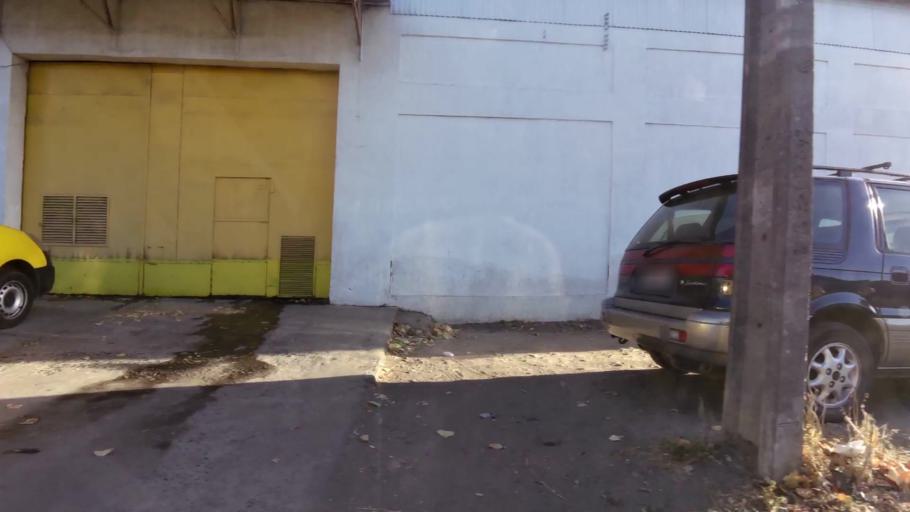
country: CL
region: Maule
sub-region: Provincia de Talca
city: Talca
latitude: -35.4330
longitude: -71.6437
